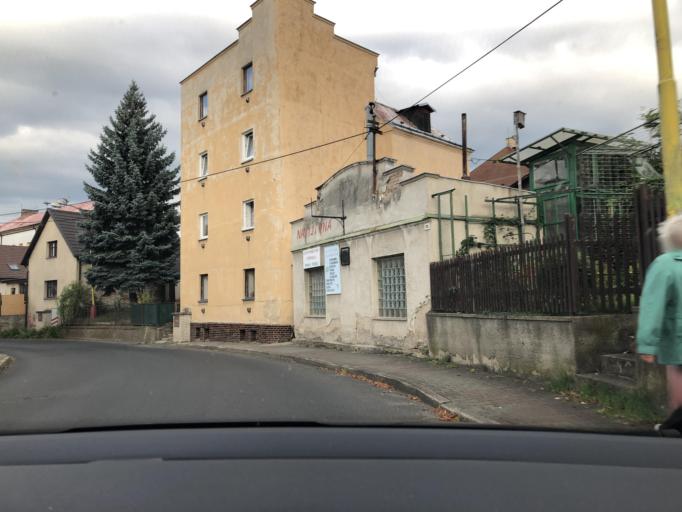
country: CZ
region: Ustecky
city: Velke Brezno
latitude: 50.6618
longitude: 14.1411
